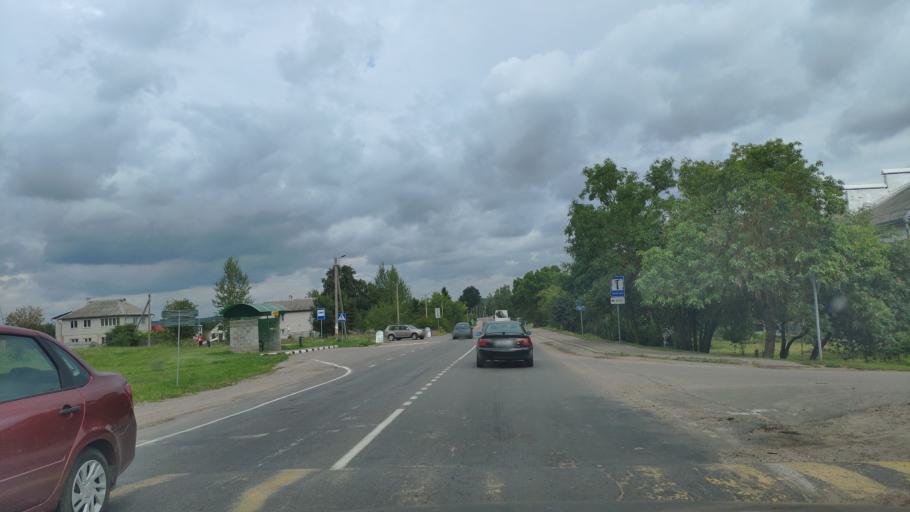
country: BY
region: Minsk
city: Zaslawye
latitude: 53.9945
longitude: 27.2703
